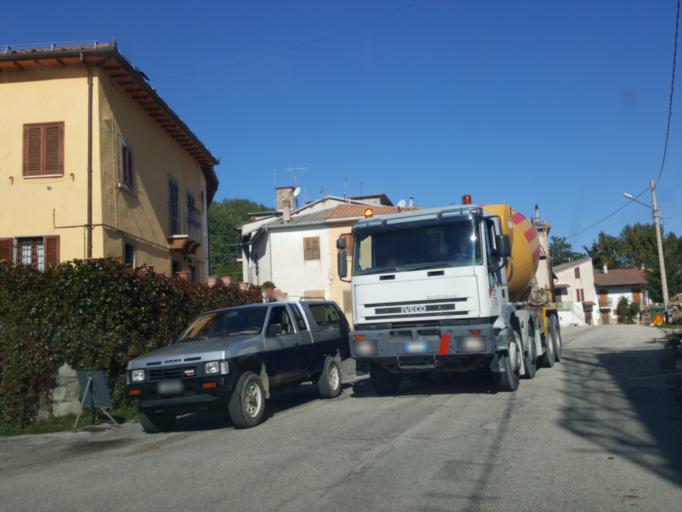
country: IT
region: Abruzzo
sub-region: Provincia dell' Aquila
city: Campotosto
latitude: 42.5599
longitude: 13.3277
